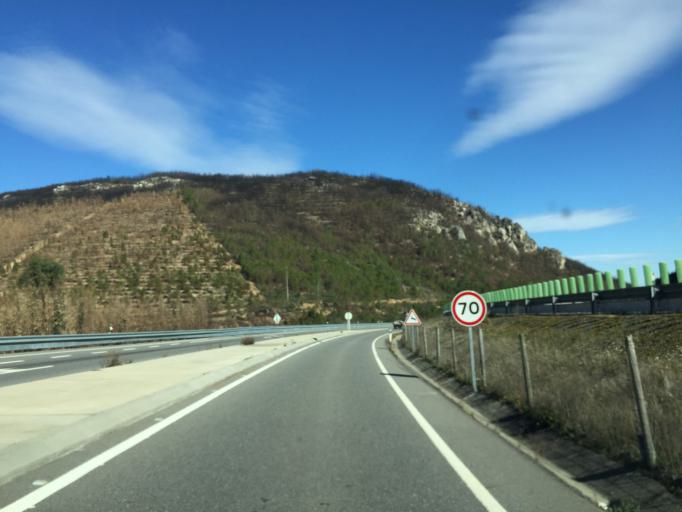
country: PT
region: Portalegre
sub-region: Nisa
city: Nisa
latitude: 39.6927
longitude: -7.7143
